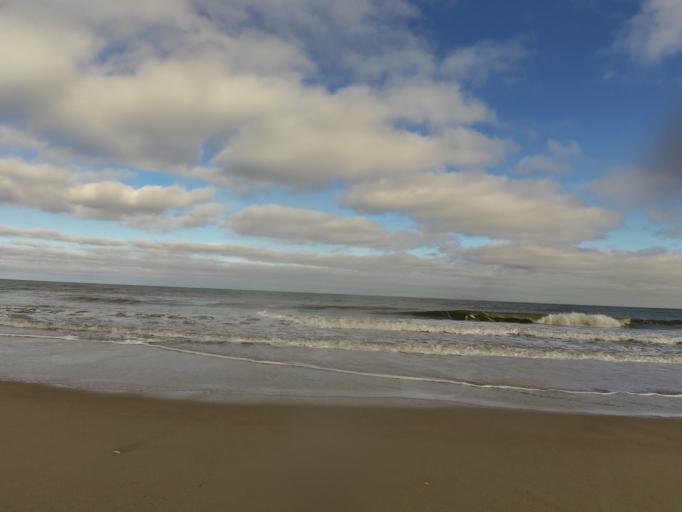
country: US
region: Florida
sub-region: Nassau County
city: Fernandina Beach
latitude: 30.5614
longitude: -81.4425
